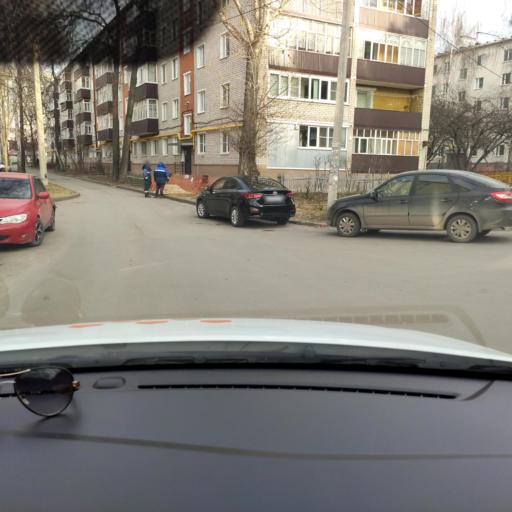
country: RU
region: Tatarstan
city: Vysokaya Gora
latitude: 55.8586
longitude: 49.2259
